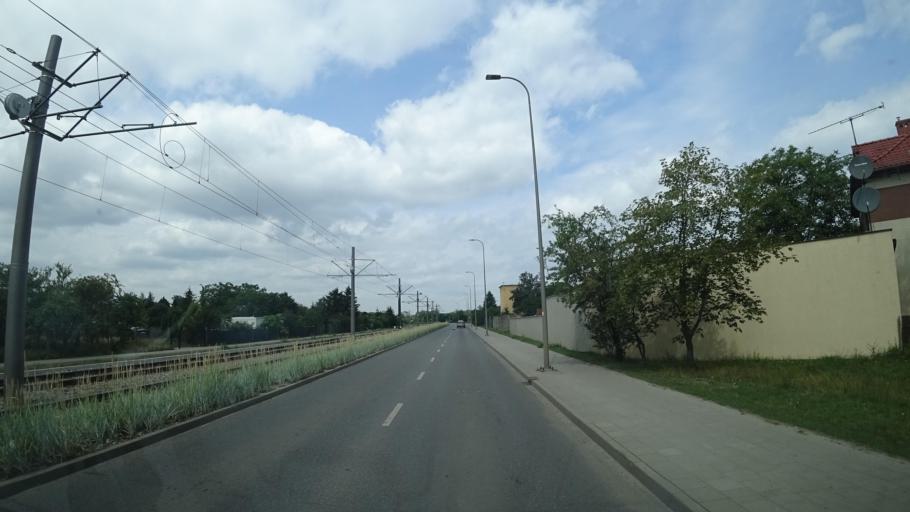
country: PL
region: Pomeranian Voivodeship
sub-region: Gdansk
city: Gdansk
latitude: 54.3617
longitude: 18.7085
